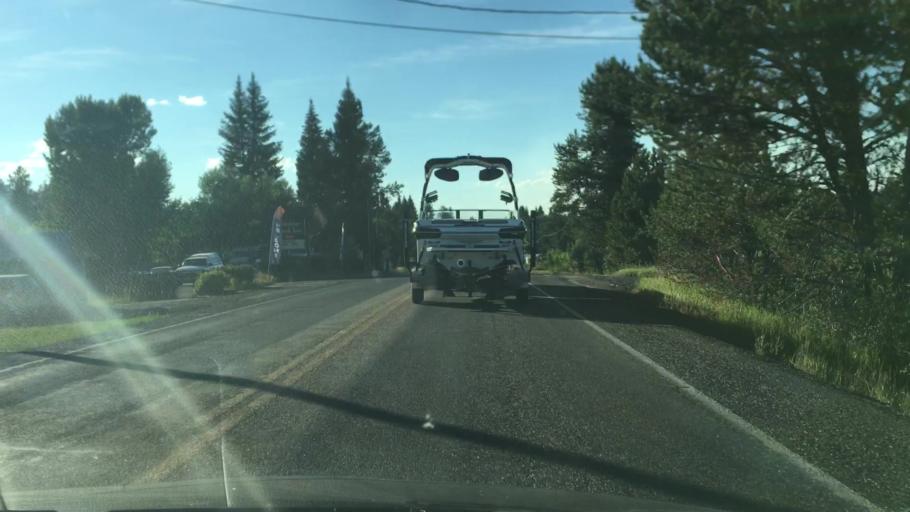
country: US
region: Idaho
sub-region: Valley County
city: McCall
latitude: 44.7254
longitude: -116.0726
